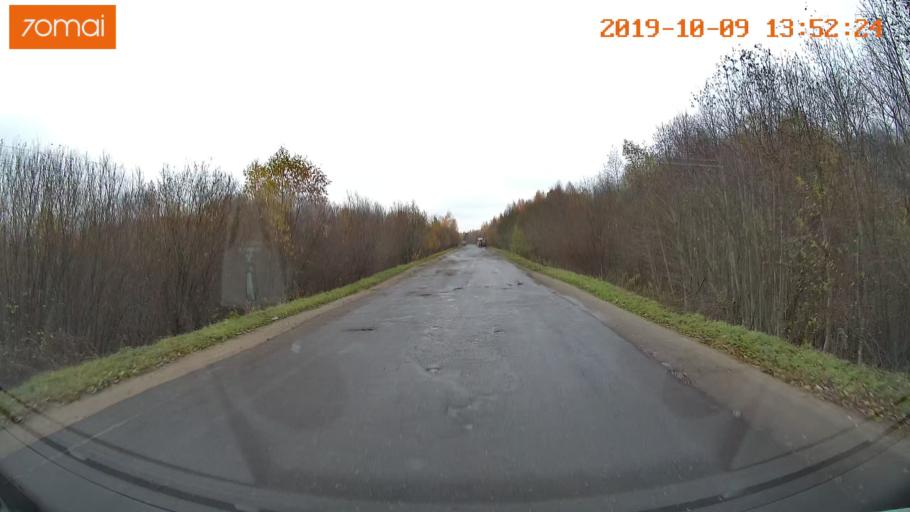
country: RU
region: Kostroma
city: Buy
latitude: 58.4117
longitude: 41.2490
